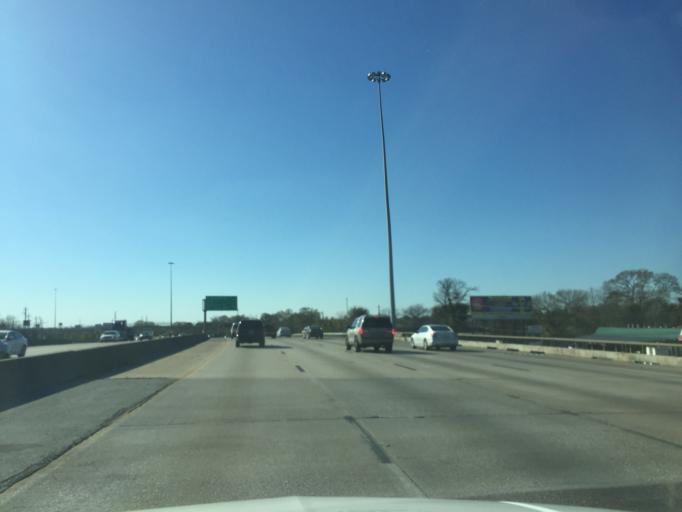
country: US
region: Texas
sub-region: Harris County
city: South Houston
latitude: 29.6971
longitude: -95.3102
